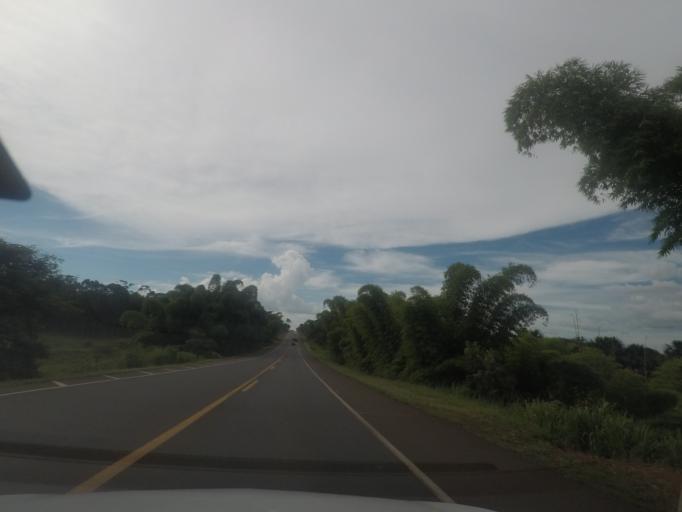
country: BR
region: Minas Gerais
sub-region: Prata
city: Prata
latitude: -19.2569
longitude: -48.9244
